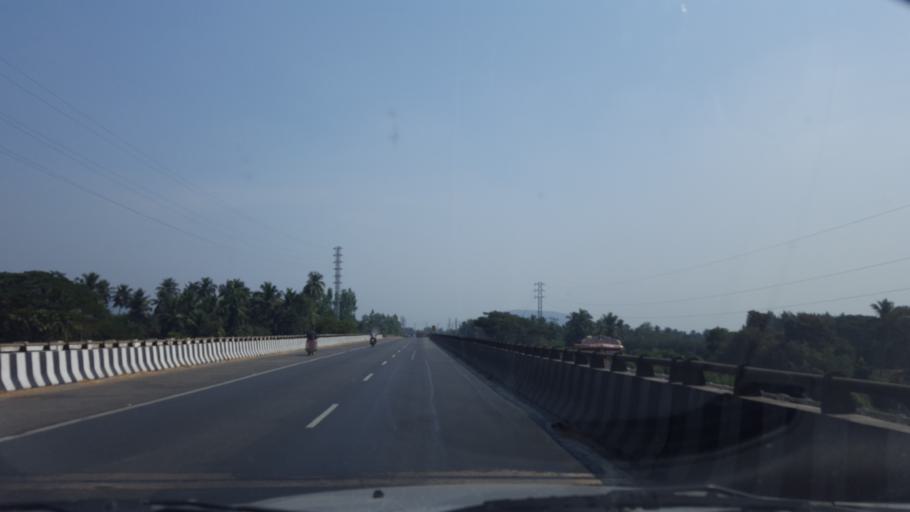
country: IN
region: Andhra Pradesh
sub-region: Vishakhapatnam
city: Anakapalle
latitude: 17.6799
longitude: 82.9915
